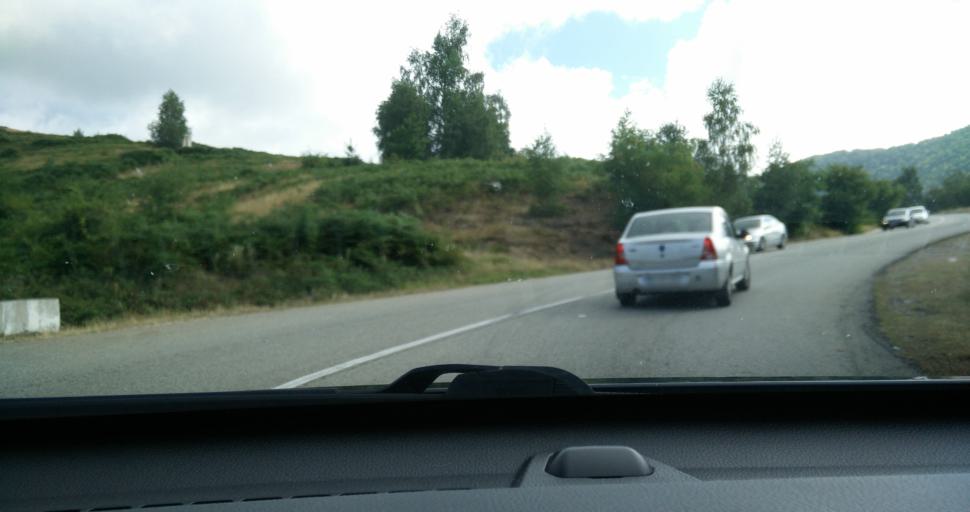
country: RO
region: Gorj
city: Novaci-Straini
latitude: 45.2094
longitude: 23.6966
